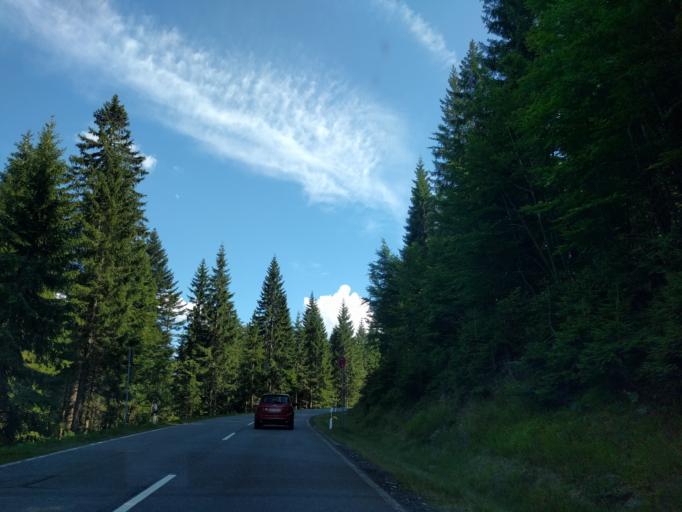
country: DE
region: Bavaria
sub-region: Lower Bavaria
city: Bayerisch Eisenstein
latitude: 49.0773
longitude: 13.1636
